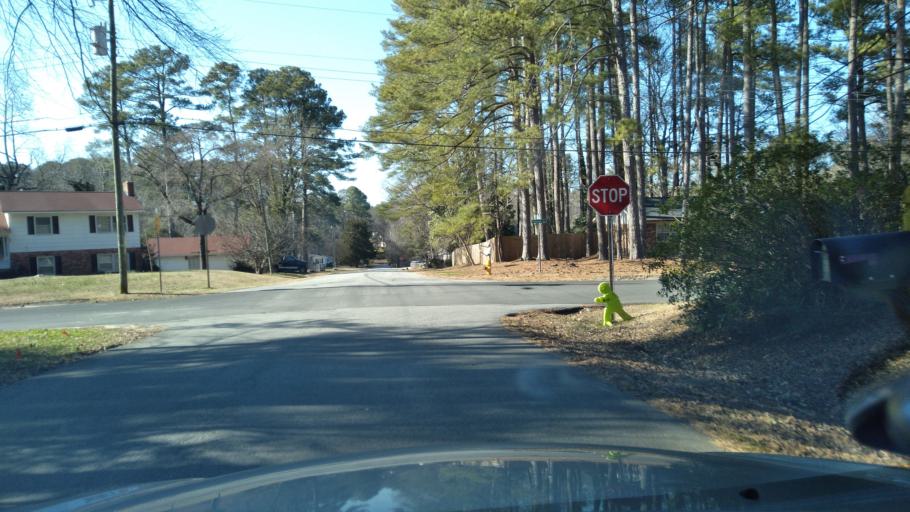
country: US
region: North Carolina
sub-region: Wake County
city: Garner
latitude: 35.6966
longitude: -78.6342
